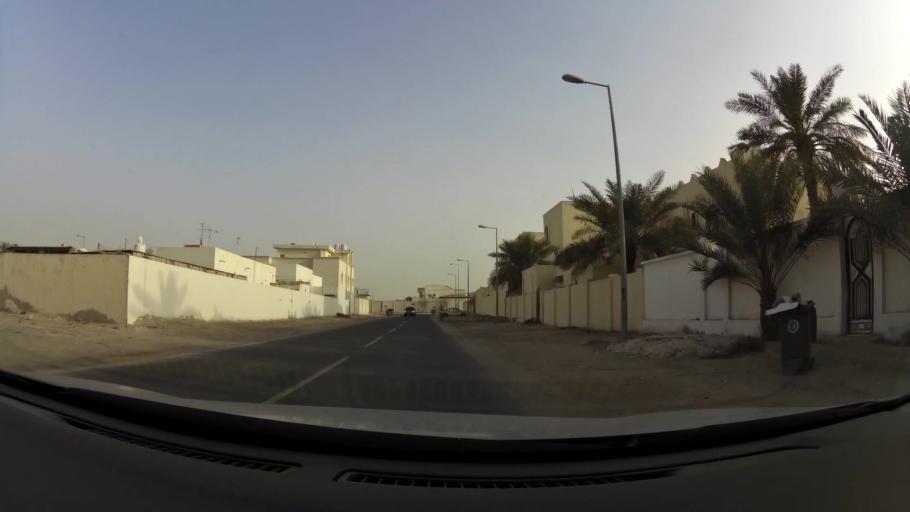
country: QA
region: Baladiyat ar Rayyan
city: Ar Rayyan
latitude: 25.2519
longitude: 51.4472
